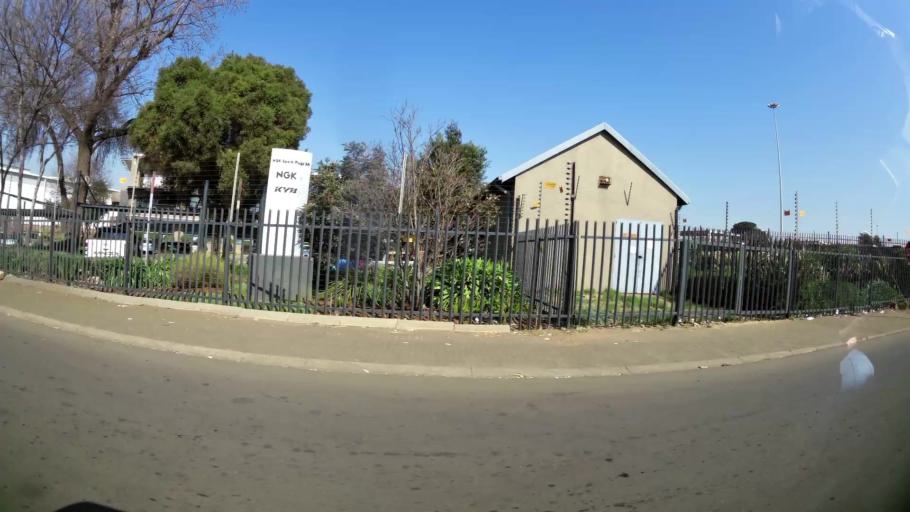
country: ZA
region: Gauteng
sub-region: Ekurhuleni Metropolitan Municipality
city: Boksburg
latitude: -26.1674
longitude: 28.2096
